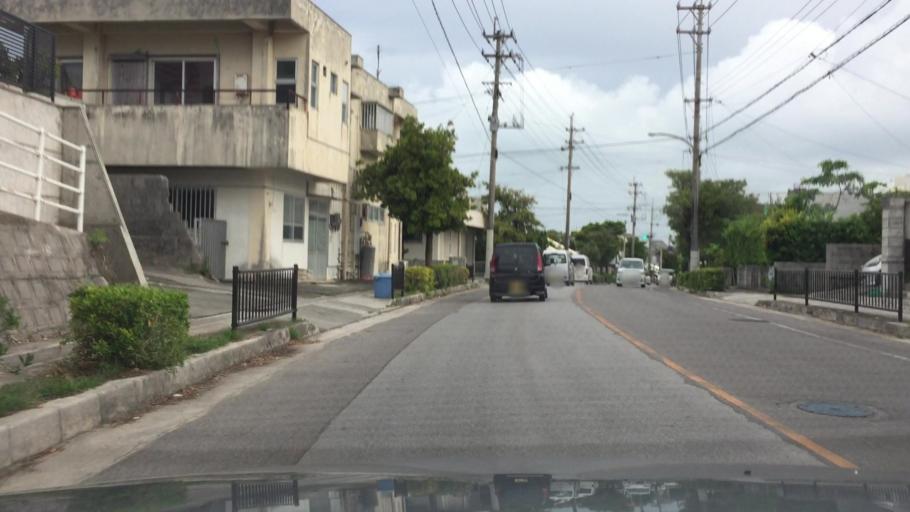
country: JP
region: Okinawa
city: Ishigaki
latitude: 24.3468
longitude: 124.1576
